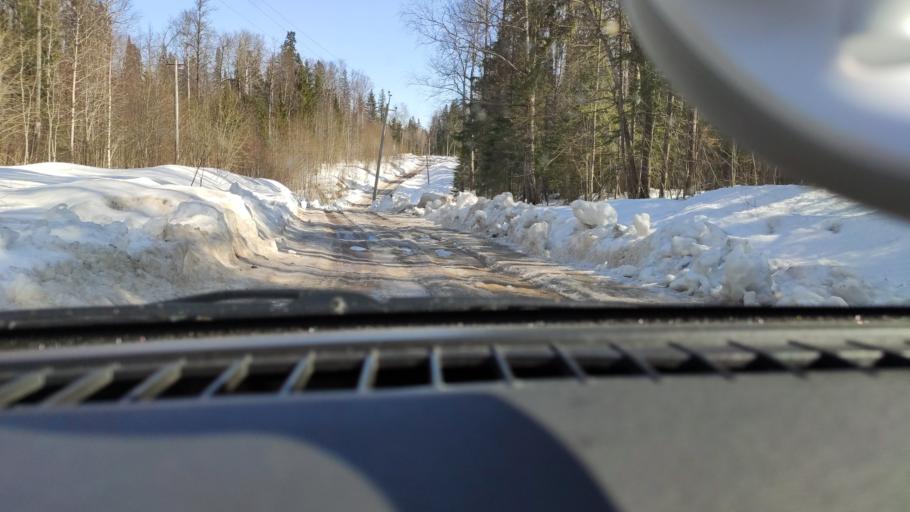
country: RU
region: Perm
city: Perm
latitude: 58.2201
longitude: 56.1608
